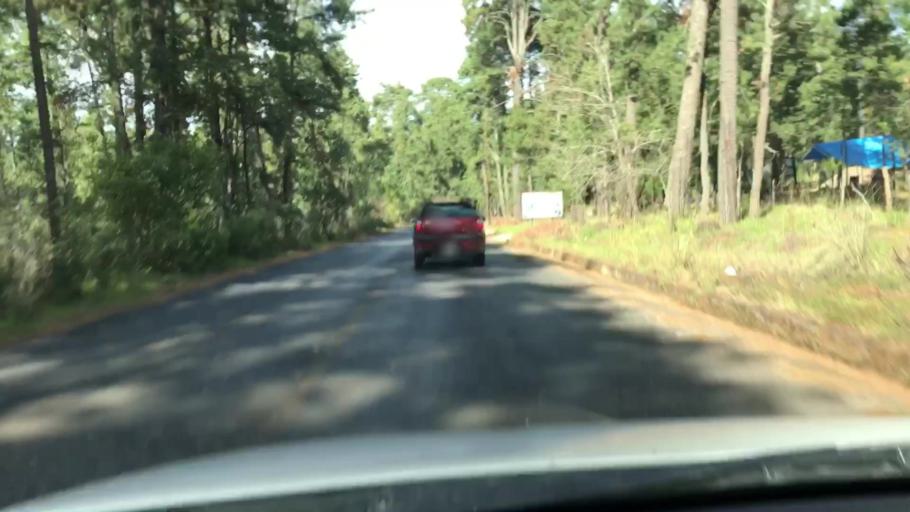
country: MX
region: Jalisco
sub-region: Amacueca
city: Tepec
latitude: 20.0860
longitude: -103.7157
